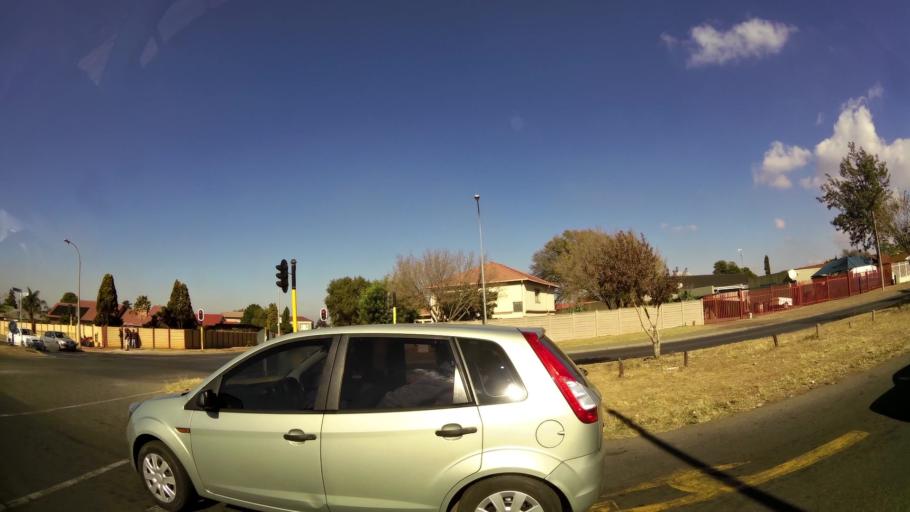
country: ZA
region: Gauteng
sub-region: City of Johannesburg Metropolitan Municipality
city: Roodepoort
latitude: -26.1519
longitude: 27.8306
